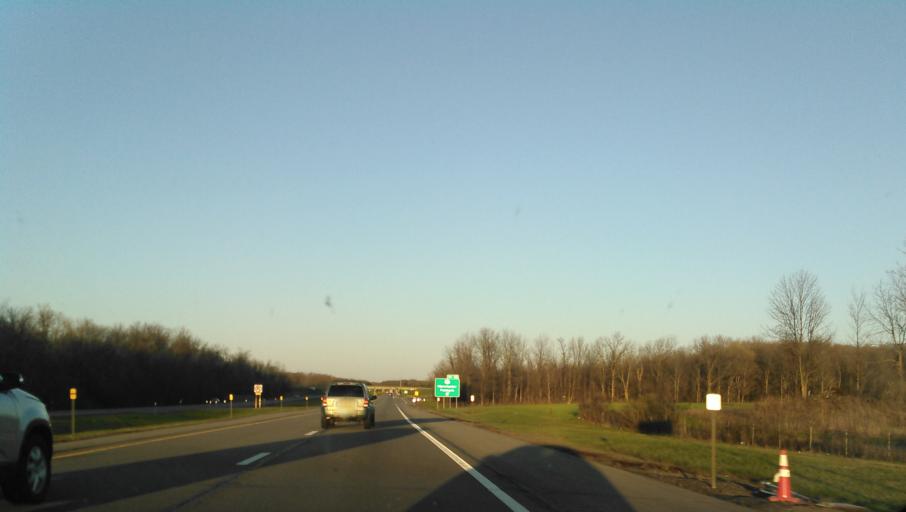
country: US
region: New York
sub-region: Ontario County
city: Manchester
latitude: 42.9788
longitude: -77.2417
